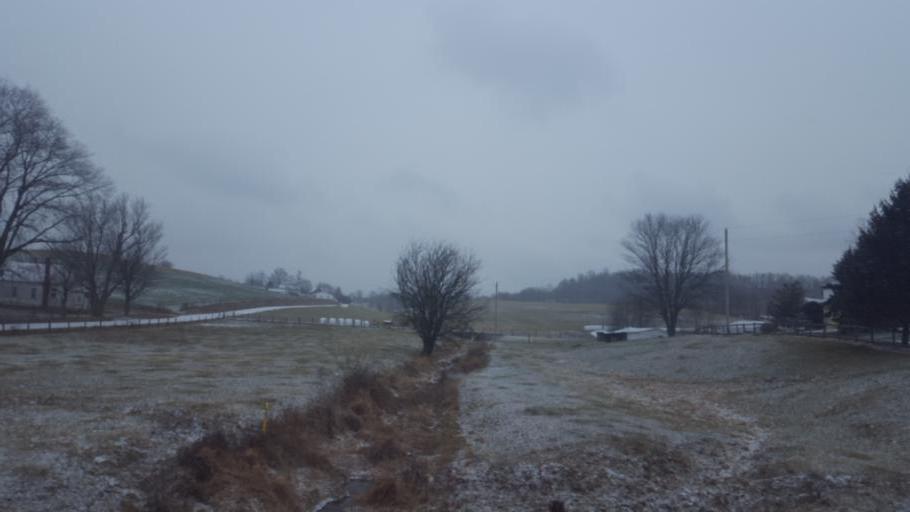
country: US
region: Ohio
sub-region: Tuscarawas County
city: Sugarcreek
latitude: 40.4601
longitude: -81.7428
